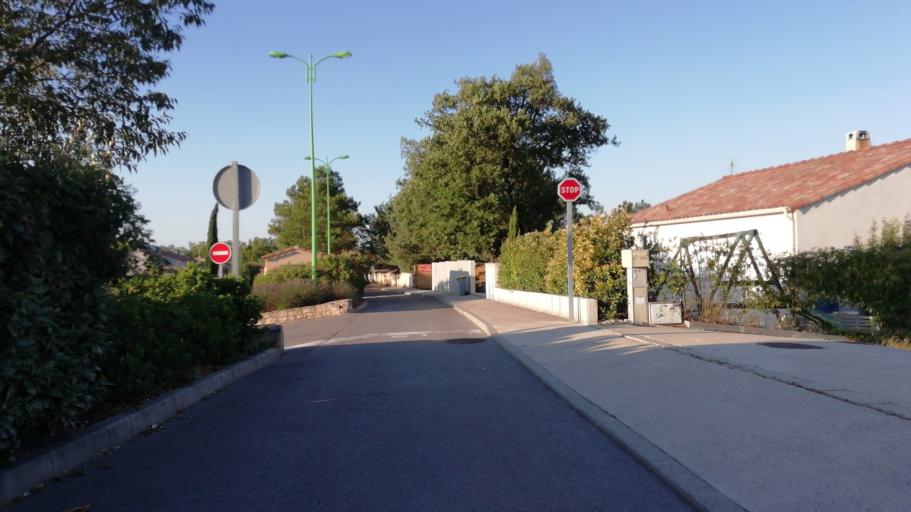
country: FR
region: Languedoc-Roussillon
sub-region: Departement de l'Herault
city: Saint-Martin-de-Londres
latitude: 43.7840
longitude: 3.7335
